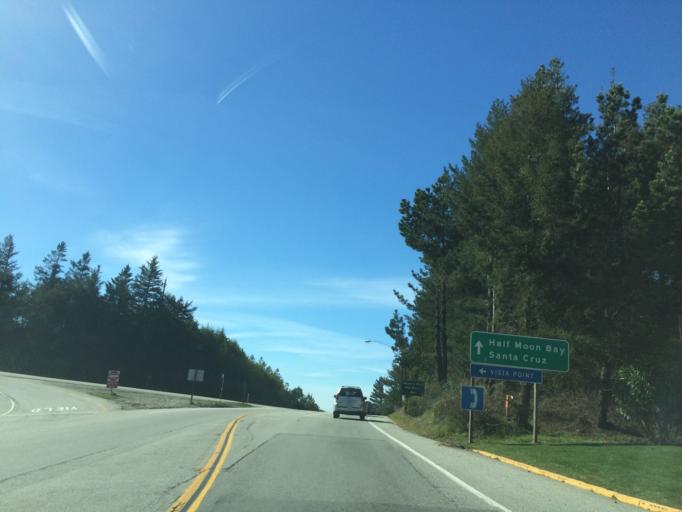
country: US
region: California
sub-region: San Mateo County
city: Highlands-Baywood Park
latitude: 37.4961
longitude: -122.3682
